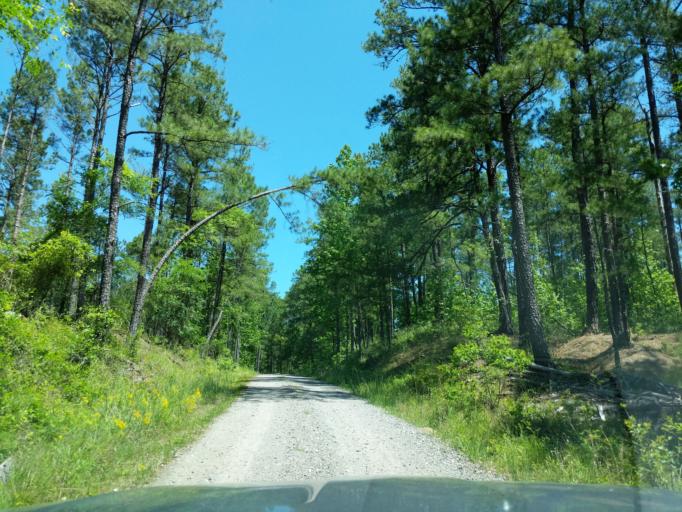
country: US
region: Georgia
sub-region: Columbia County
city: Evans
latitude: 33.6157
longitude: -82.1140
